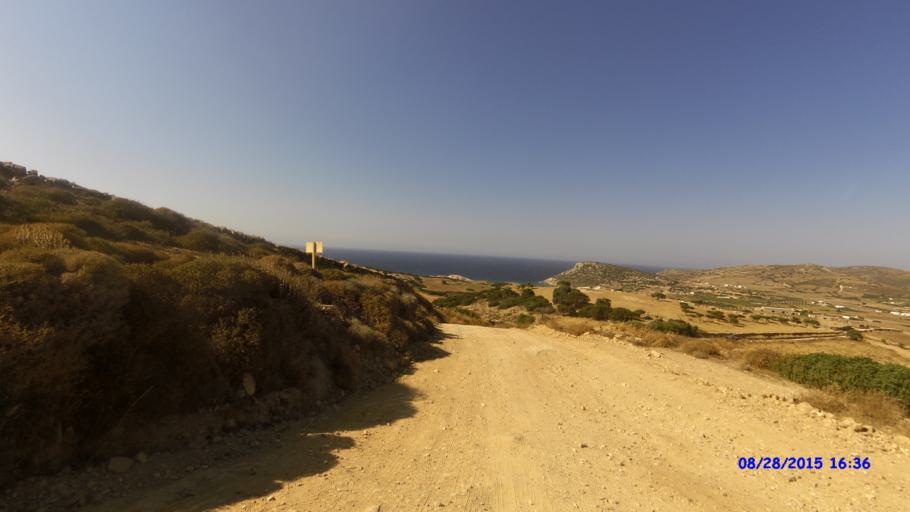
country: GR
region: South Aegean
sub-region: Nomos Kykladon
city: Antiparos
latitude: 37.0099
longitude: 25.0462
